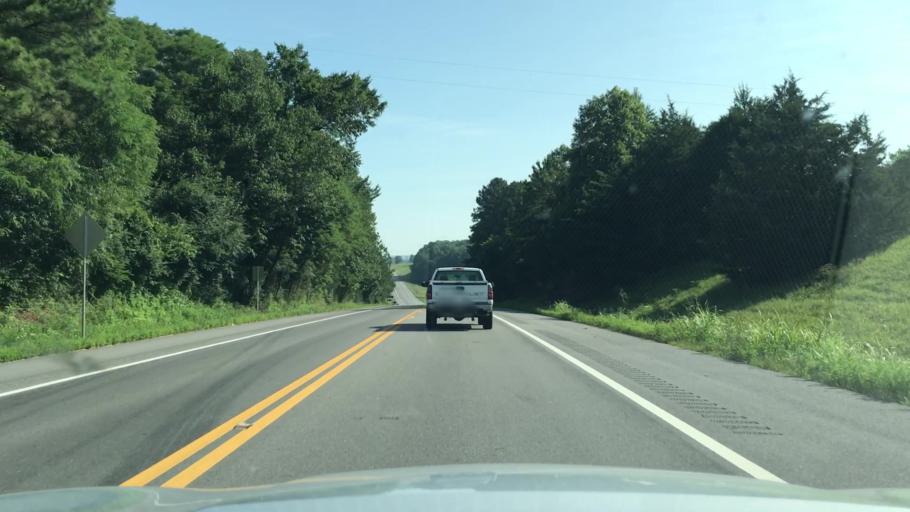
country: US
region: Tennessee
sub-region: Pickett County
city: Byrdstown
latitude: 36.4863
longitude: -85.1841
